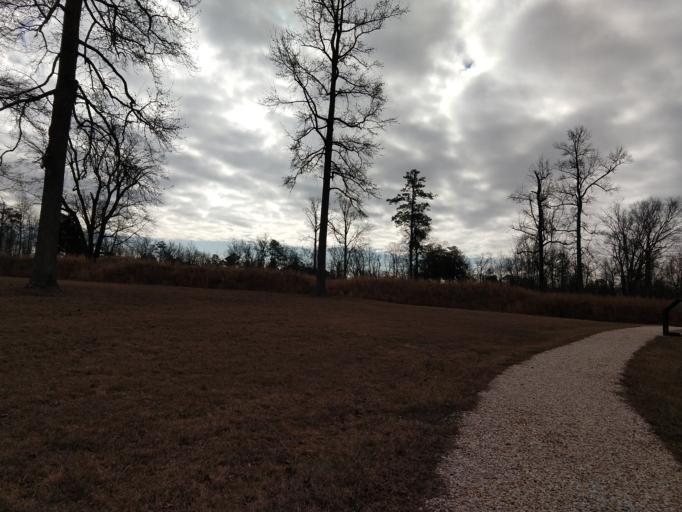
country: US
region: Virginia
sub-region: Chesterfield County
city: Bellwood
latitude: 37.4274
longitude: -77.3731
